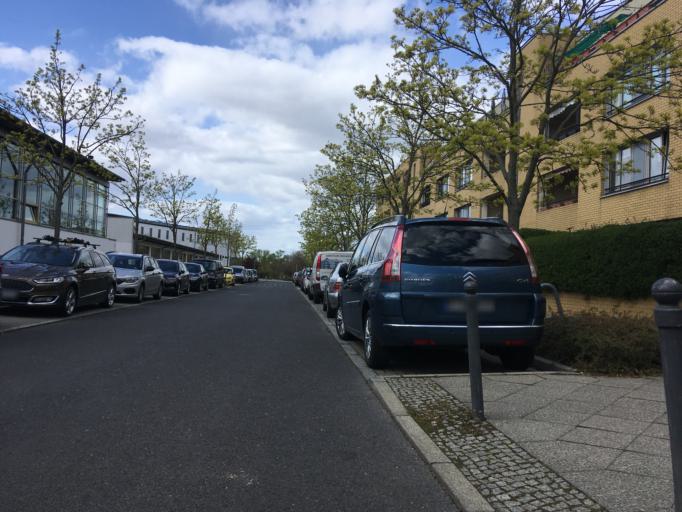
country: DE
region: Berlin
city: Altglienicke
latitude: 52.4066
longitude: 13.5385
